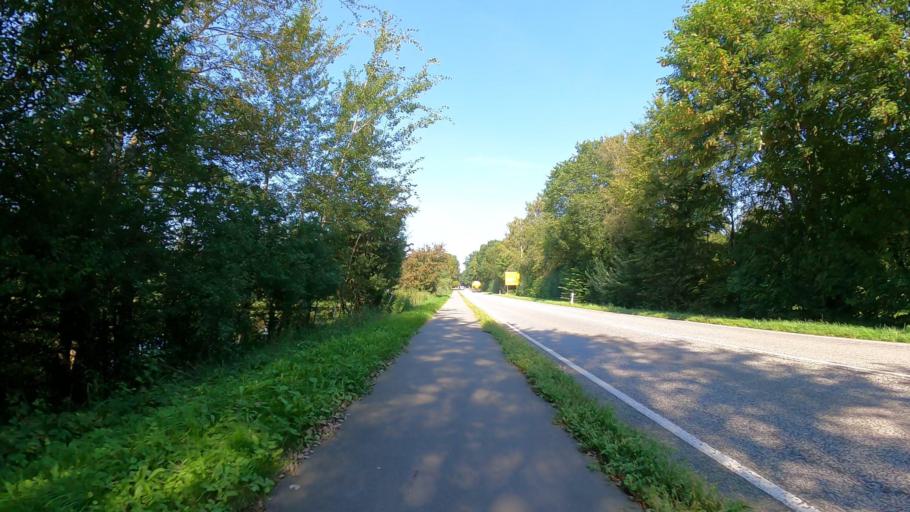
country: DE
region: Schleswig-Holstein
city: Bad Bramstedt
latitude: 53.8987
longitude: 9.8837
